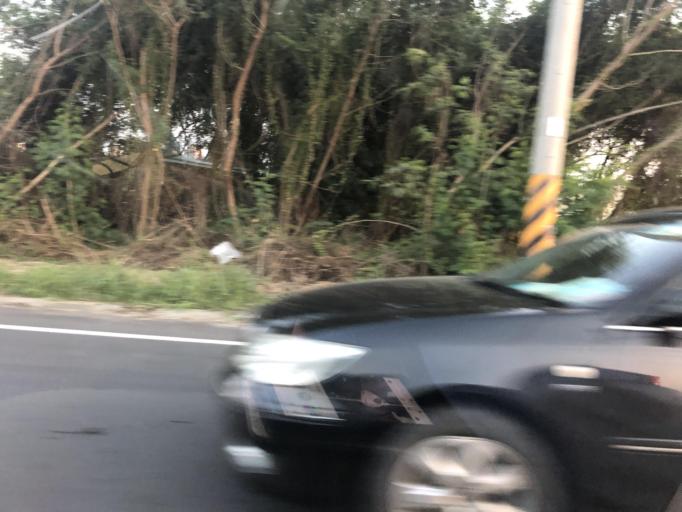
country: TW
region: Taiwan
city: Xinying
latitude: 23.3003
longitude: 120.2923
